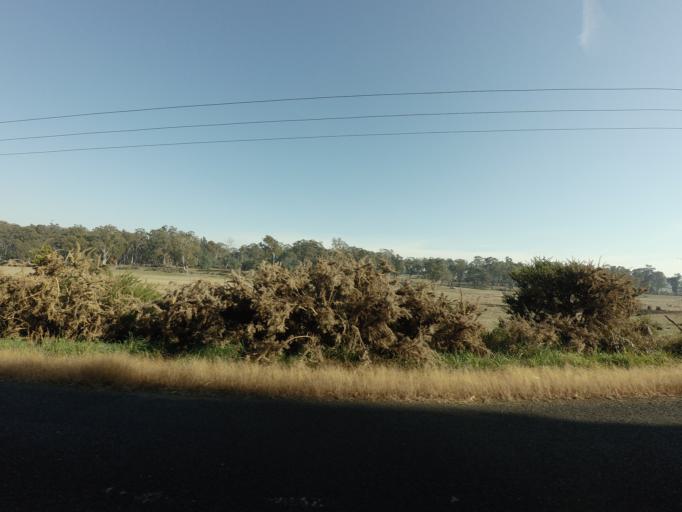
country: AU
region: Tasmania
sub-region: Northern Midlands
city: Longford
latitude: -41.5501
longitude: 146.9906
